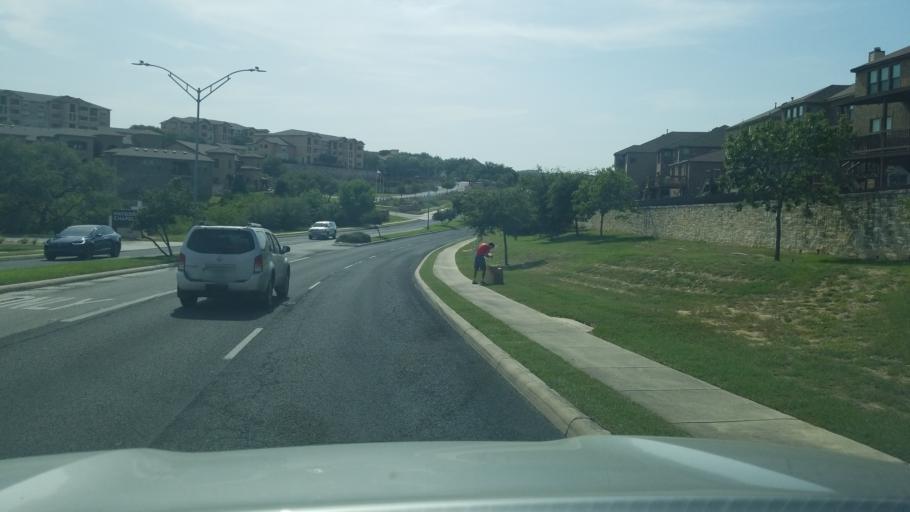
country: US
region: Texas
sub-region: Bexar County
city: Hollywood Park
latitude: 29.6376
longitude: -98.4726
